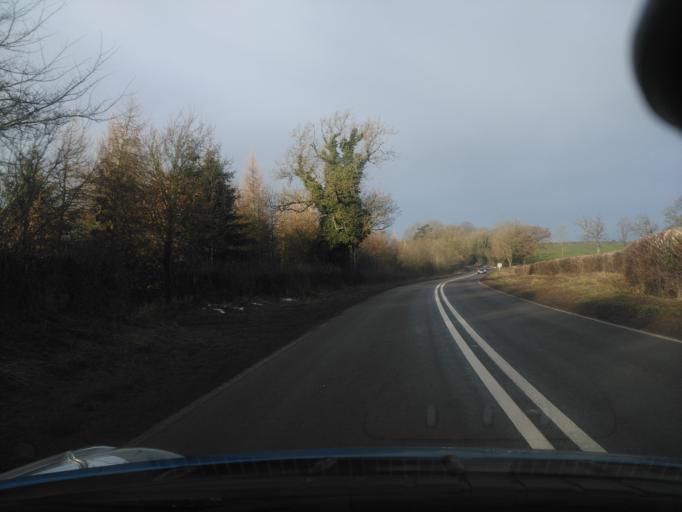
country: GB
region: England
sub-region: Oxfordshire
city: Chipping Norton
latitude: 51.9499
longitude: -1.5885
